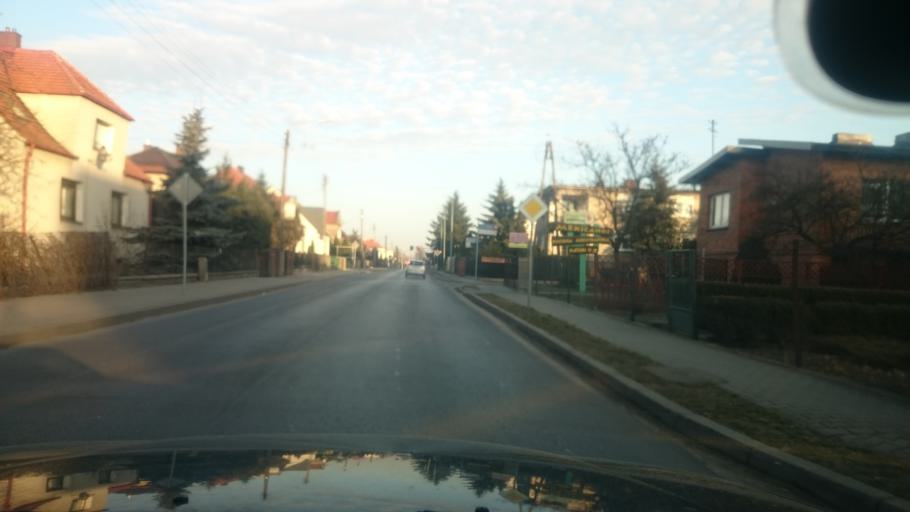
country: PL
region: Greater Poland Voivodeship
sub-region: Powiat ostrowski
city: Ostrow Wielkopolski
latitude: 51.6471
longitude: 17.8342
